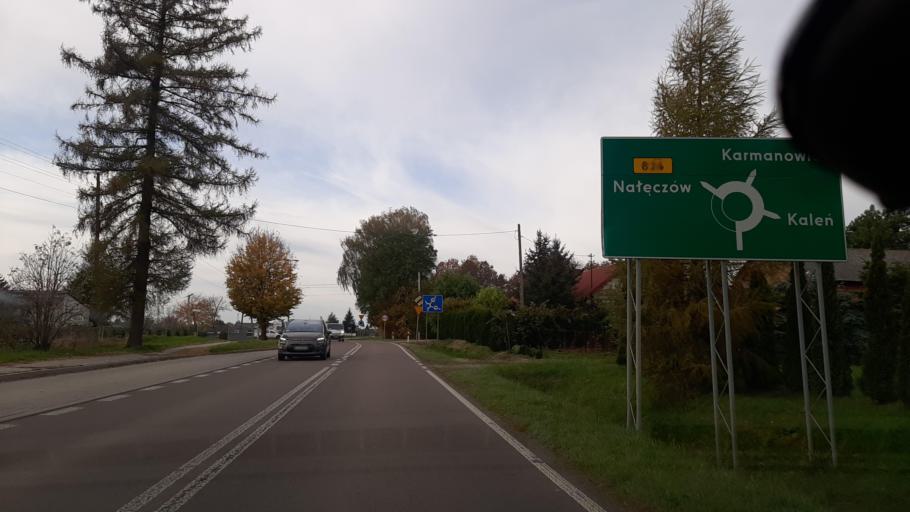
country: PL
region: Lublin Voivodeship
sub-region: Powiat pulawski
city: Naleczow
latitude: 51.3197
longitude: 22.2265
